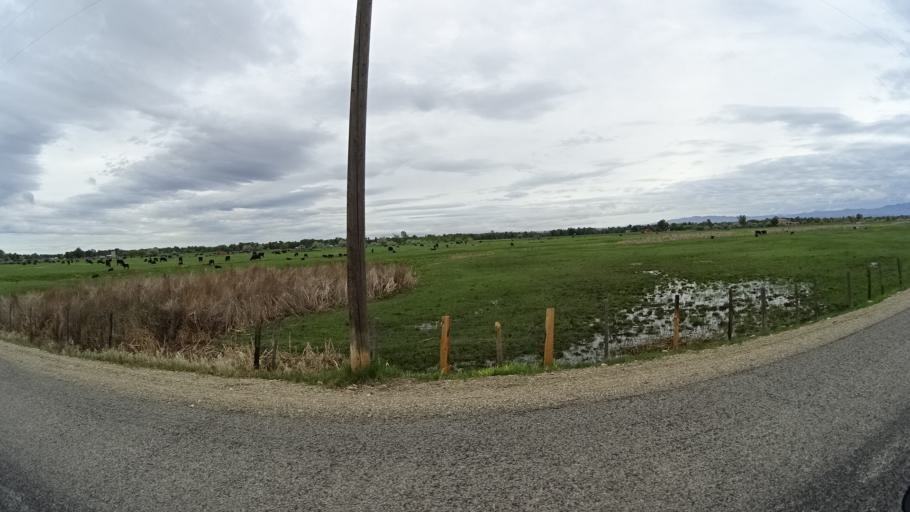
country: US
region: Idaho
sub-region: Ada County
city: Star
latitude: 43.6702
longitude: -116.4848
